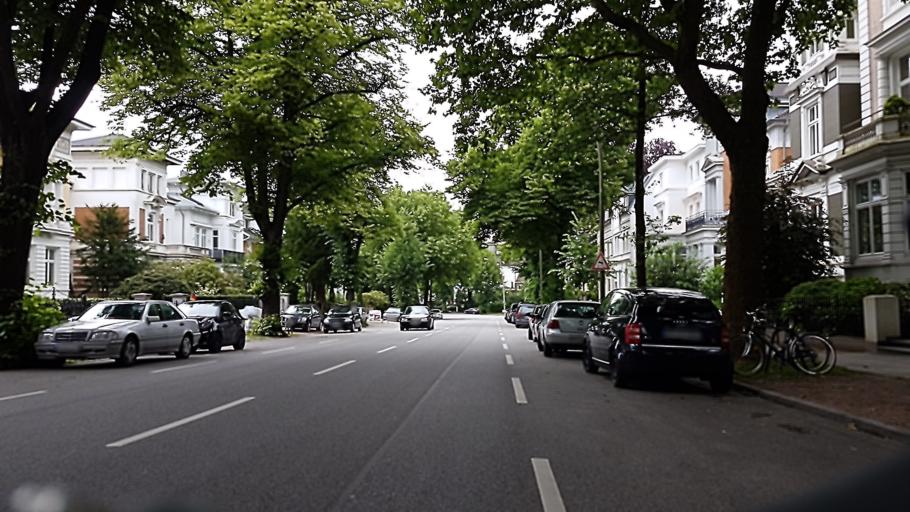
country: DE
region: Hamburg
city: Hamburg-Nord
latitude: 53.5803
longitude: 9.9942
